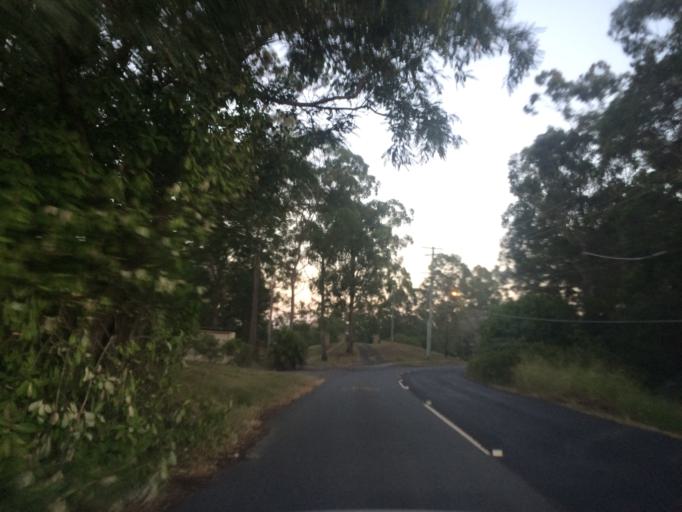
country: AU
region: Queensland
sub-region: Brisbane
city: Kenmore Hills
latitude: -27.4916
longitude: 152.9332
